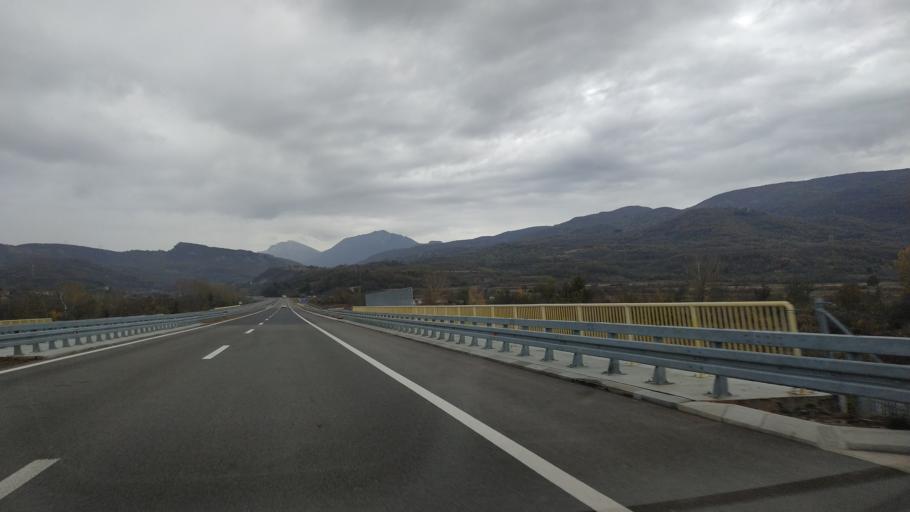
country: RS
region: Central Serbia
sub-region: Nisavski Okrug
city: Niska Banja
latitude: 43.3096
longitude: 22.0356
